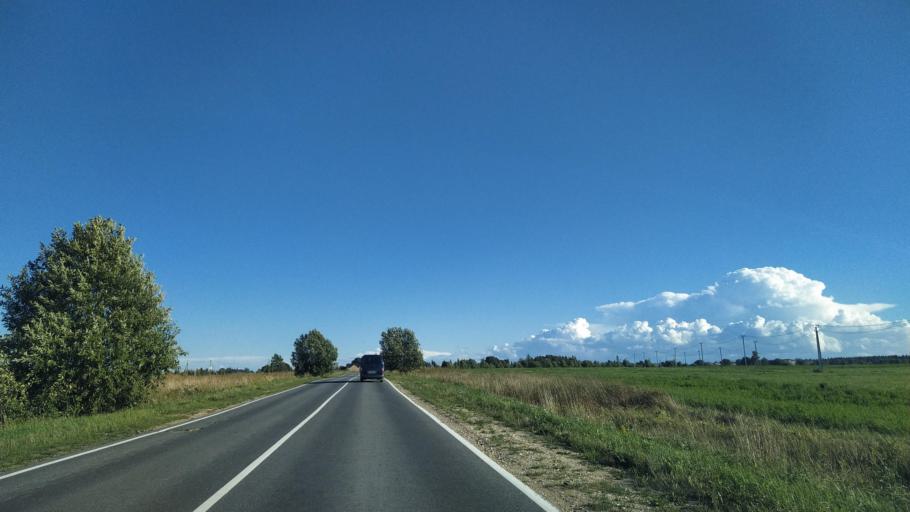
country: RU
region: Leningrad
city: Siverskiy
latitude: 59.3369
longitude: 30.0282
